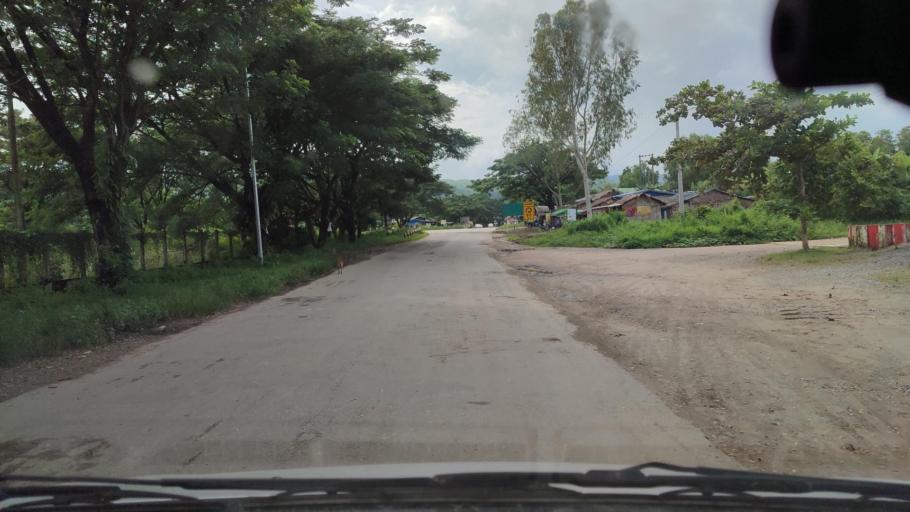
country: MM
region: Bago
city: Pyu
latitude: 18.5132
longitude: 96.3900
